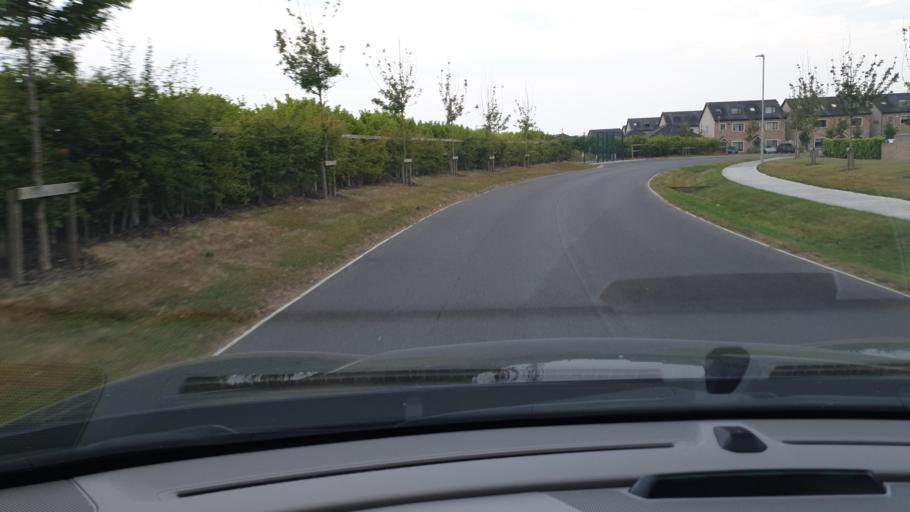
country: IE
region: Leinster
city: Donabate
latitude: 53.4960
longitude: -6.1440
